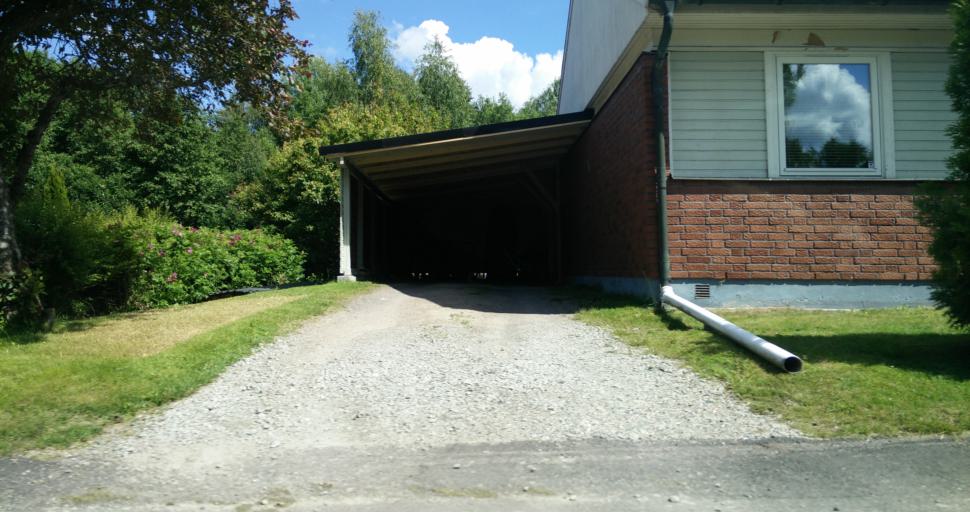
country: SE
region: Vaermland
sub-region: Hagfors Kommun
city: Hagfors
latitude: 60.0202
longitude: 13.6829
